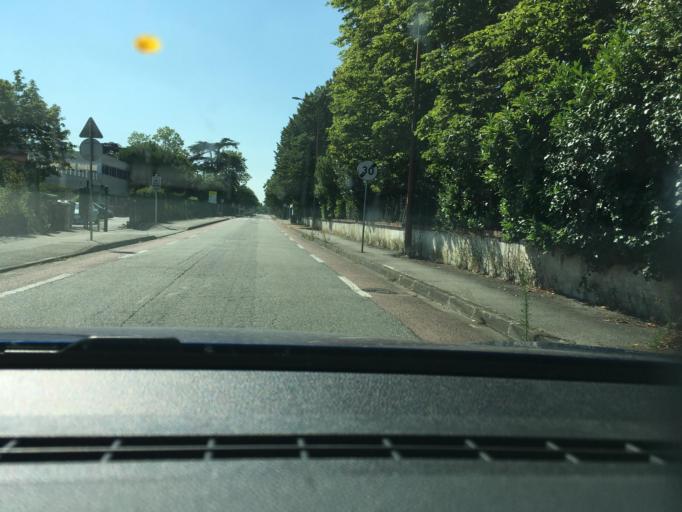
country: FR
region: Midi-Pyrenees
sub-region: Departement de la Haute-Garonne
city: Portet-sur-Garonne
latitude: 43.5663
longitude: 1.3889
